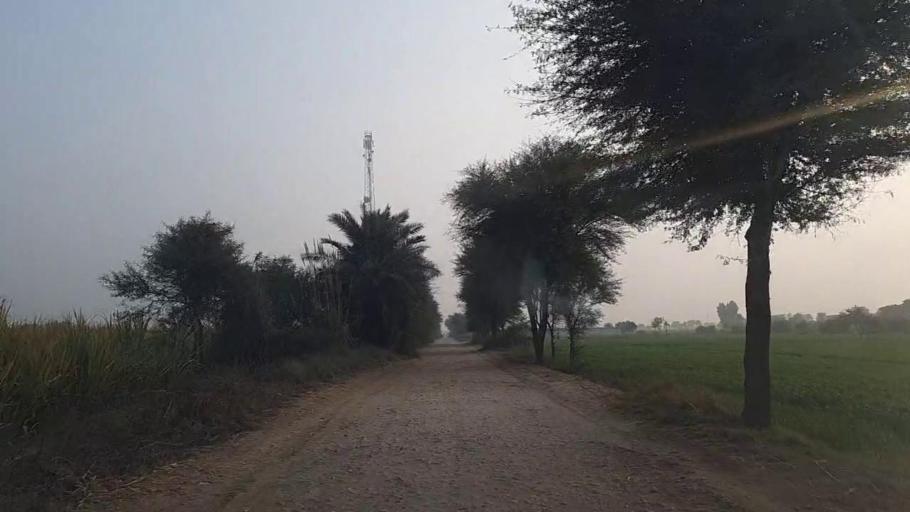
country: PK
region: Sindh
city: Khadro
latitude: 26.1227
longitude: 68.7960
